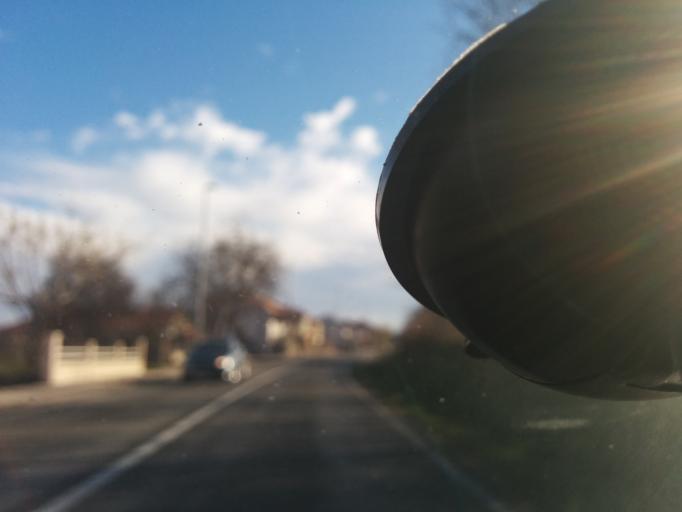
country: HR
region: Splitsko-Dalmatinska
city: Sinj
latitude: 43.6926
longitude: 16.6441
